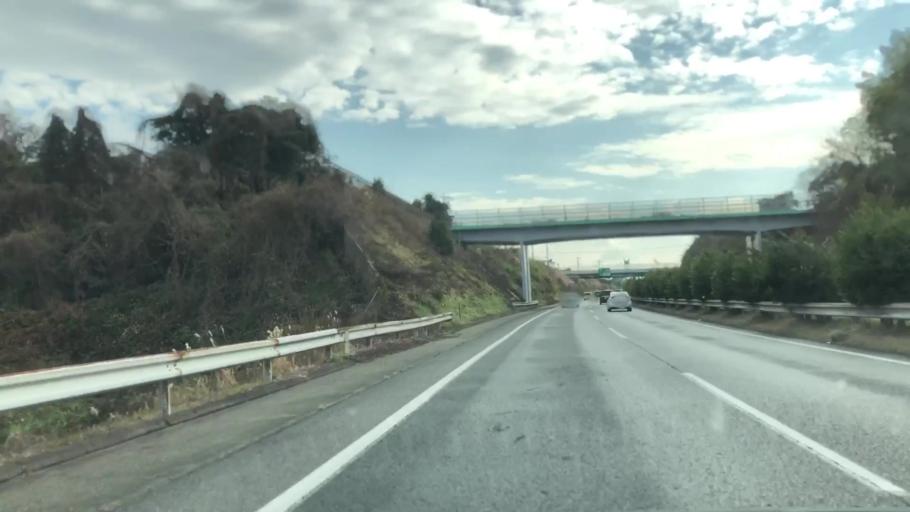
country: JP
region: Fukuoka
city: Setakamachi-takayanagi
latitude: 33.1340
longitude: 130.5167
